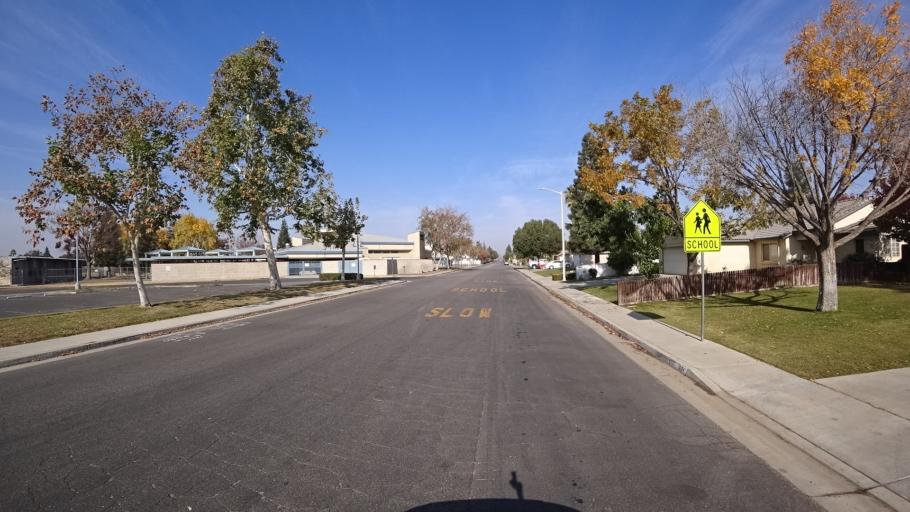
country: US
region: California
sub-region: Kern County
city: Greenacres
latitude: 35.3636
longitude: -119.1038
